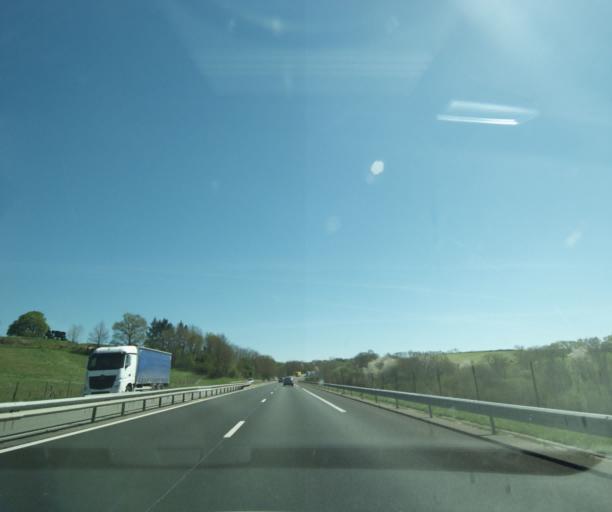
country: FR
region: Limousin
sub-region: Departement de la Haute-Vienne
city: Pierre-Buffiere
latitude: 45.7252
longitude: 1.3457
